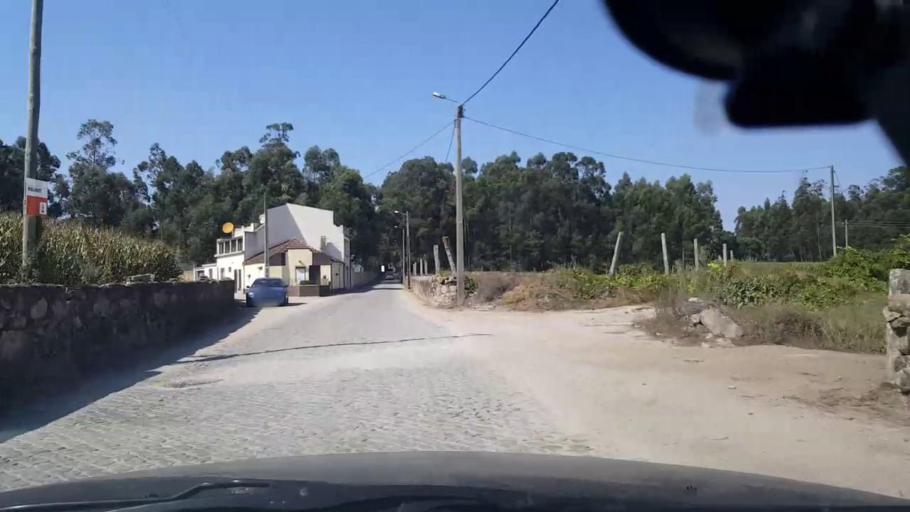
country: PT
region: Porto
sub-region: Povoa de Varzim
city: Pedroso
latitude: 41.3911
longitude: -8.7122
